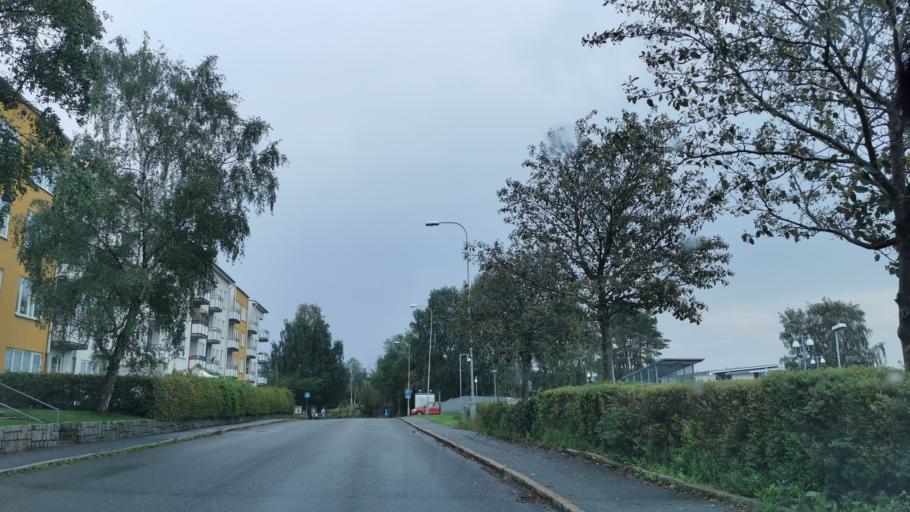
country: SE
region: Vaestra Goetaland
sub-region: Goteborg
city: Majorna
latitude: 57.6728
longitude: 11.9120
